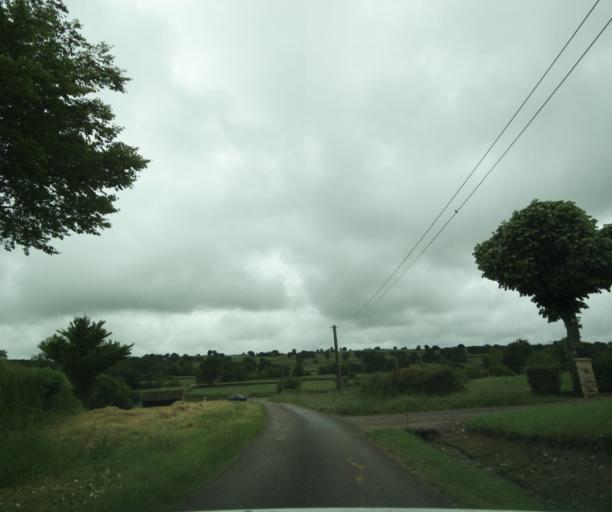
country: FR
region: Bourgogne
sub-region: Departement de Saone-et-Loire
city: Charolles
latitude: 46.4612
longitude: 4.3126
